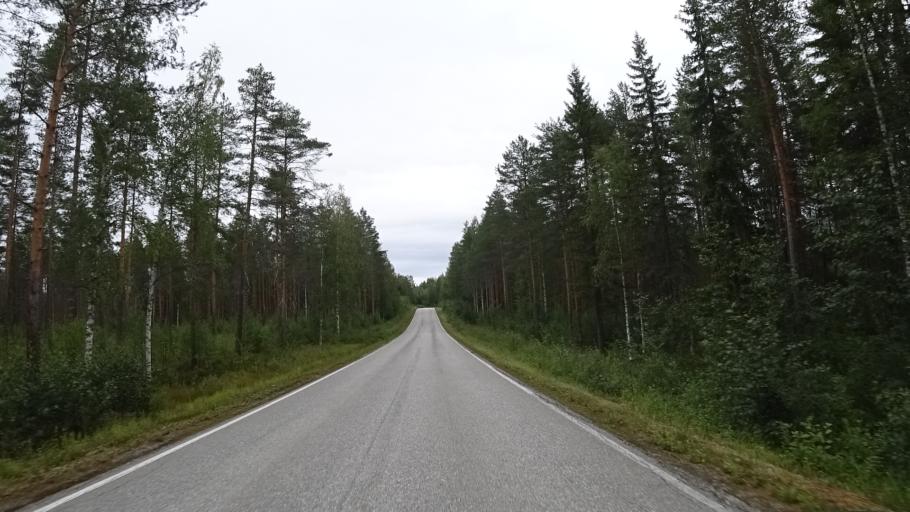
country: FI
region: North Karelia
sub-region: Pielisen Karjala
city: Lieksa
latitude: 63.3718
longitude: 30.2993
